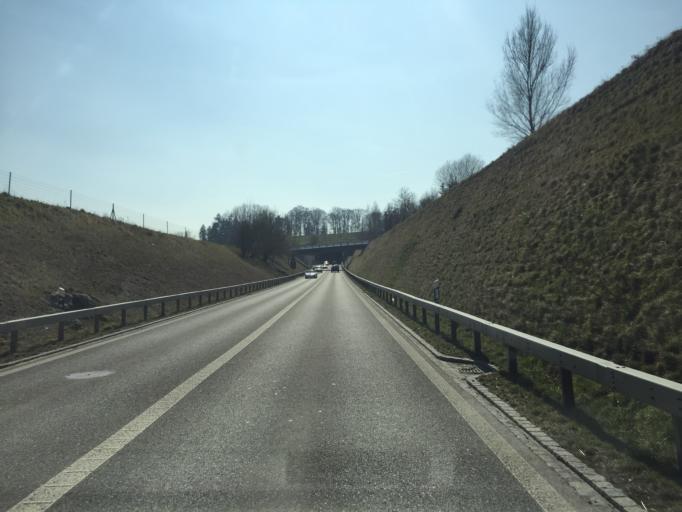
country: CH
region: Saint Gallen
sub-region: Wahlkreis Wil
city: Jonschwil
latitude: 47.4131
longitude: 9.0724
